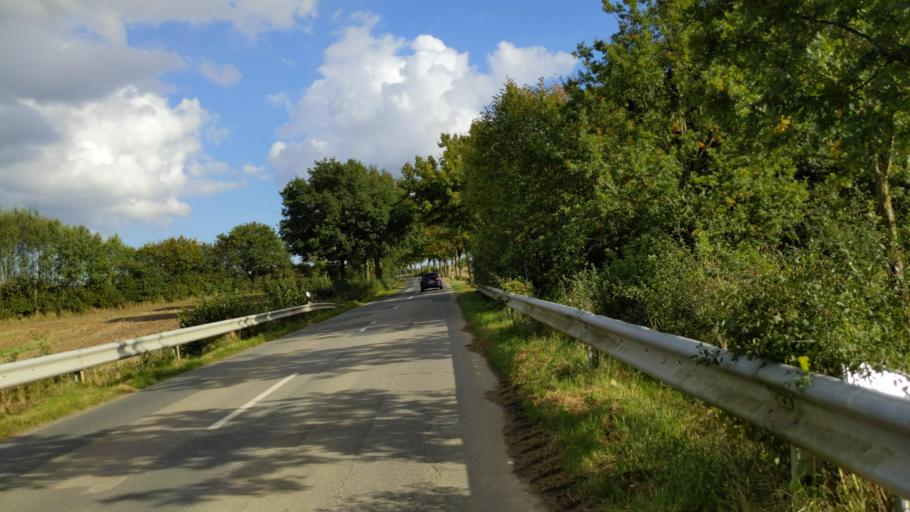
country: DE
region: Schleswig-Holstein
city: Ahrensbok
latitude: 54.0194
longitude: 10.6087
